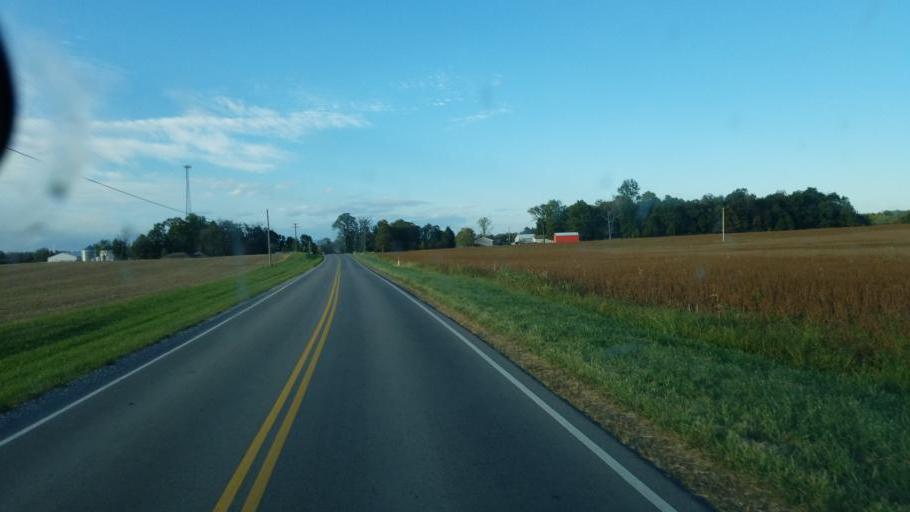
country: US
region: Ohio
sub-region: Licking County
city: Pataskala
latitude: 40.0460
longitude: -82.7333
